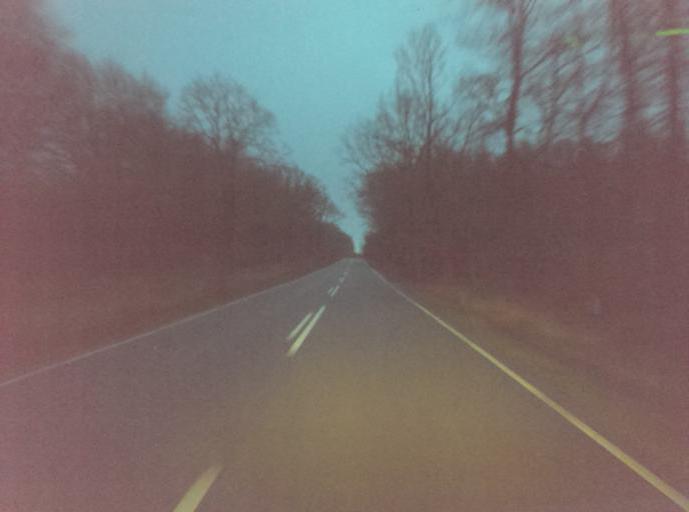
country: DK
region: South Denmark
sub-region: Esbjerg Kommune
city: Tjaereborg
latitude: 55.4879
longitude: 8.5789
